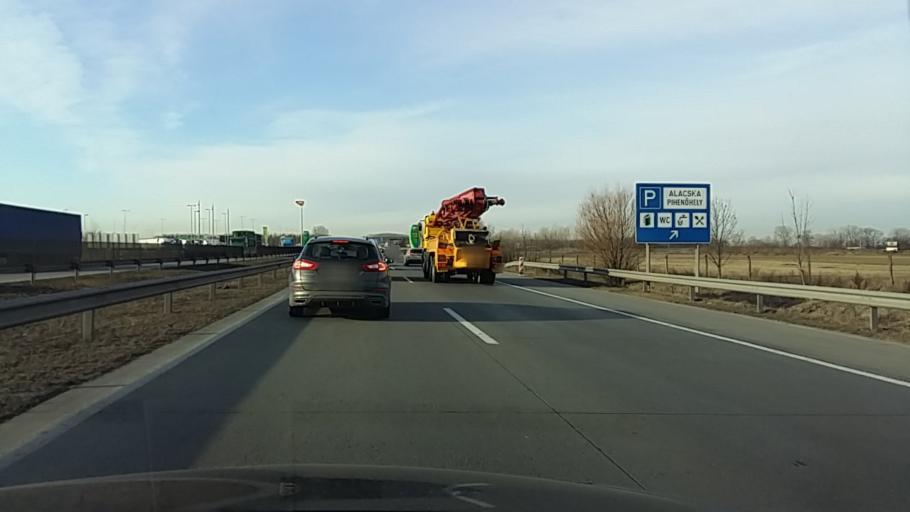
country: HU
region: Pest
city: Vecses
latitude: 47.3870
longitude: 19.2857
